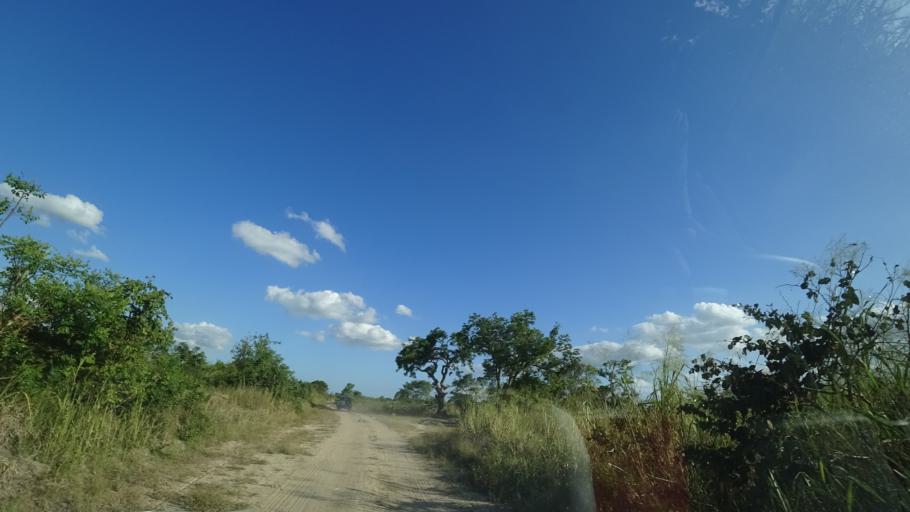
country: MZ
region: Sofala
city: Dondo
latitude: -19.3815
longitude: 34.5923
